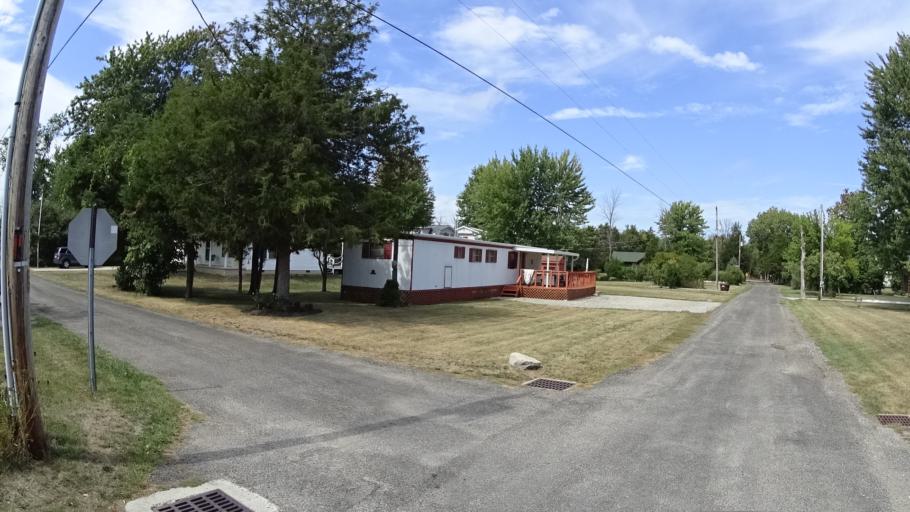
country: US
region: Ohio
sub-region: Erie County
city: Sandusky
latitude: 41.5917
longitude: -82.6909
